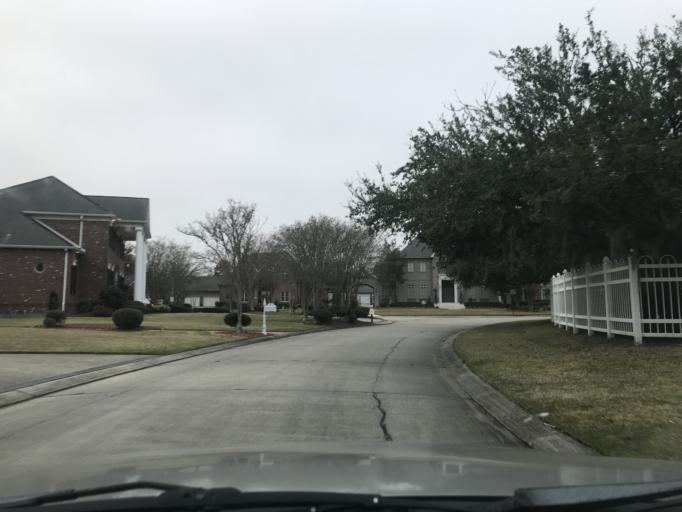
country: US
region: Louisiana
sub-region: Jefferson Parish
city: Woodmere
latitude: 29.8678
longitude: -90.0935
